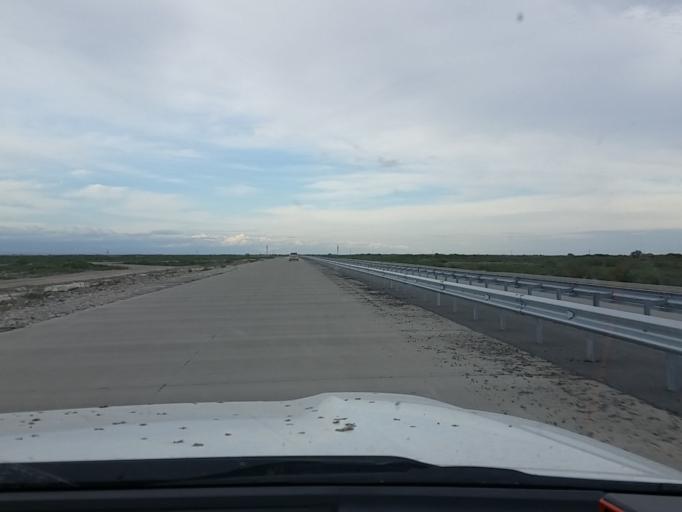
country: KZ
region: Almaty Oblysy
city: Zharkent
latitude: 44.0518
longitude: 80.0018
